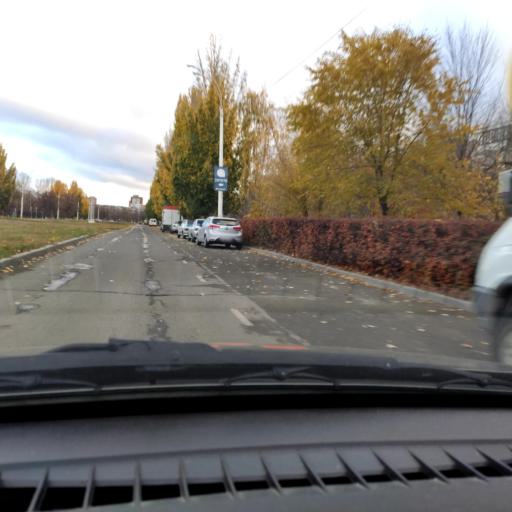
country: RU
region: Samara
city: Tol'yatti
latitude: 53.5150
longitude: 49.2854
